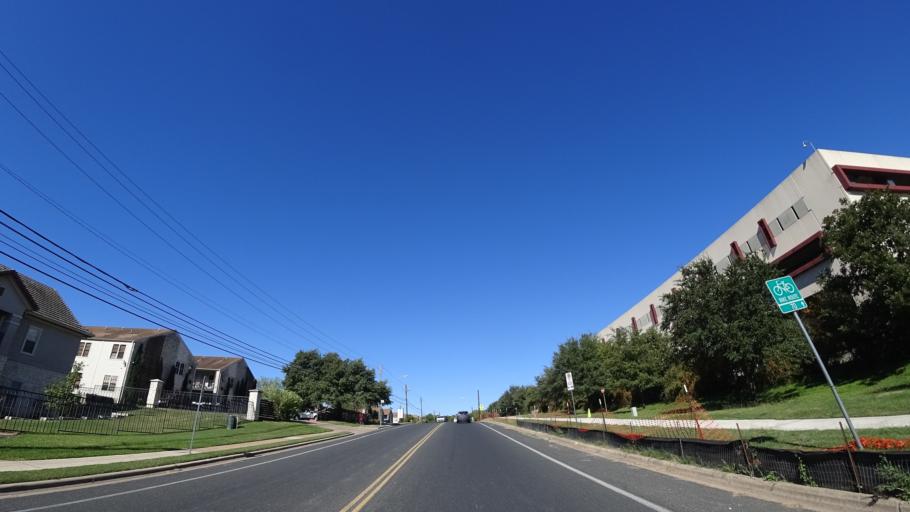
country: US
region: Texas
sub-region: Travis County
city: Austin
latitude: 30.2259
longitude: -97.7522
